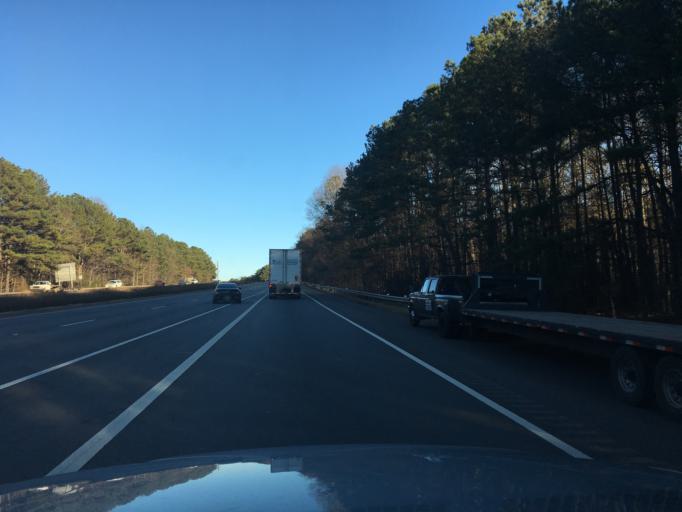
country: US
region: Georgia
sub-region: Carroll County
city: Carrollton
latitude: 33.5575
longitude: -85.0695
